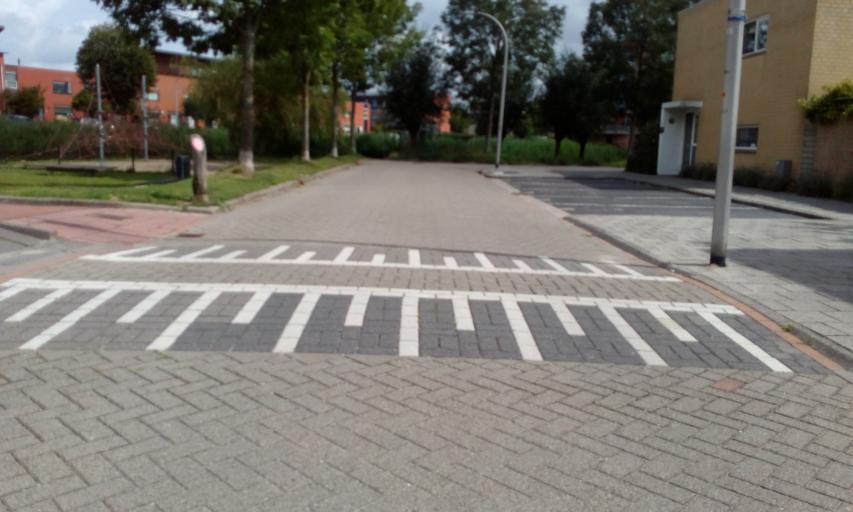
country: NL
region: South Holland
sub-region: Gemeente Delft
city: Delft
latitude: 52.0057
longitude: 4.3927
